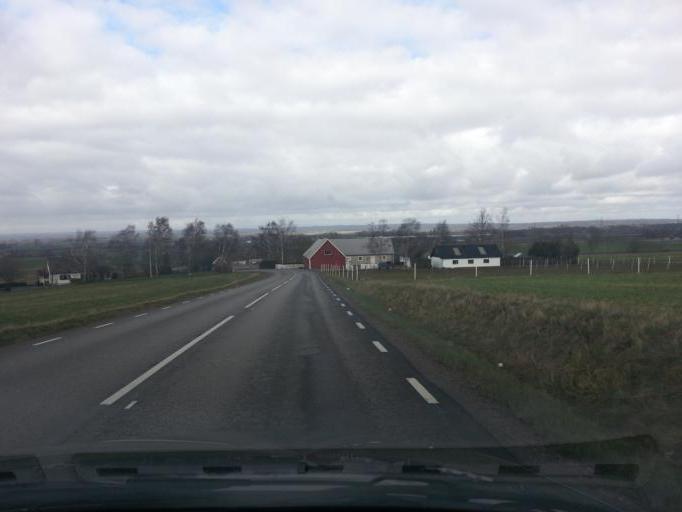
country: SE
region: Skane
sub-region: Astorps Kommun
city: Astorp
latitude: 56.1251
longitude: 12.9991
